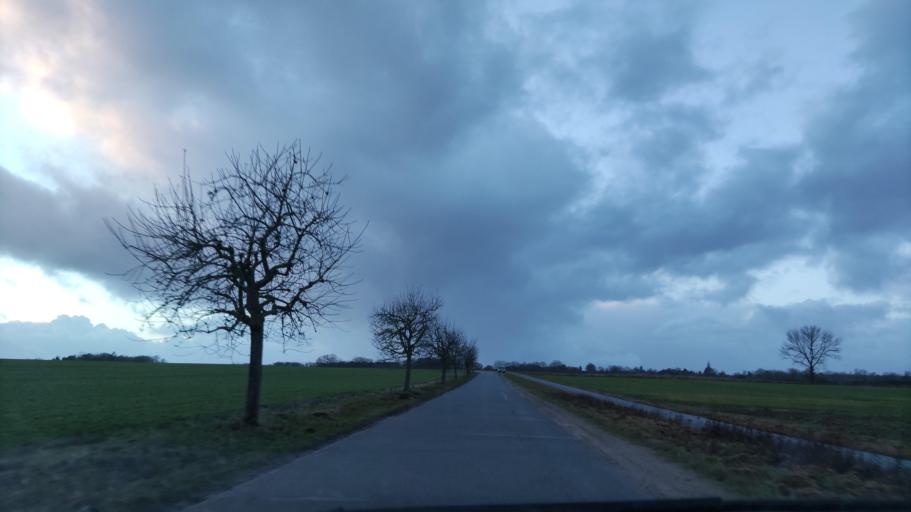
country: DE
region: Lower Saxony
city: Sudergellersen
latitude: 53.2071
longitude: 10.3137
